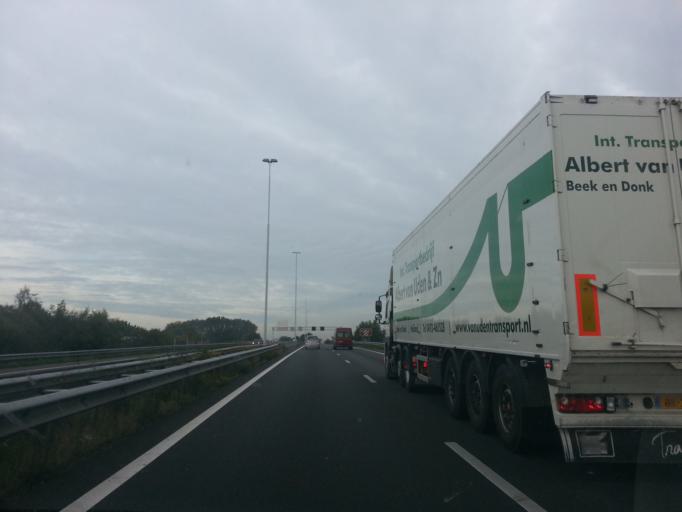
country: NL
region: North Brabant
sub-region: Gemeente Oirschot
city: Oirschot
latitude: 51.4988
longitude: 5.2989
